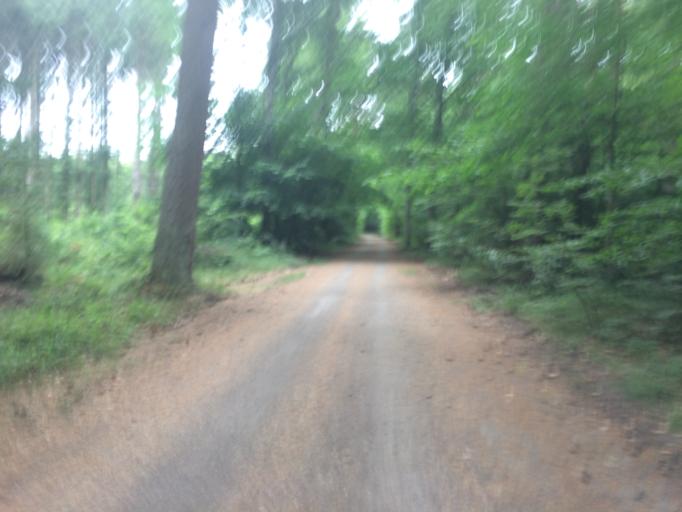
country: DK
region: Capital Region
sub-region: Bornholm Kommune
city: Ronne
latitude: 55.1366
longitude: 14.7166
